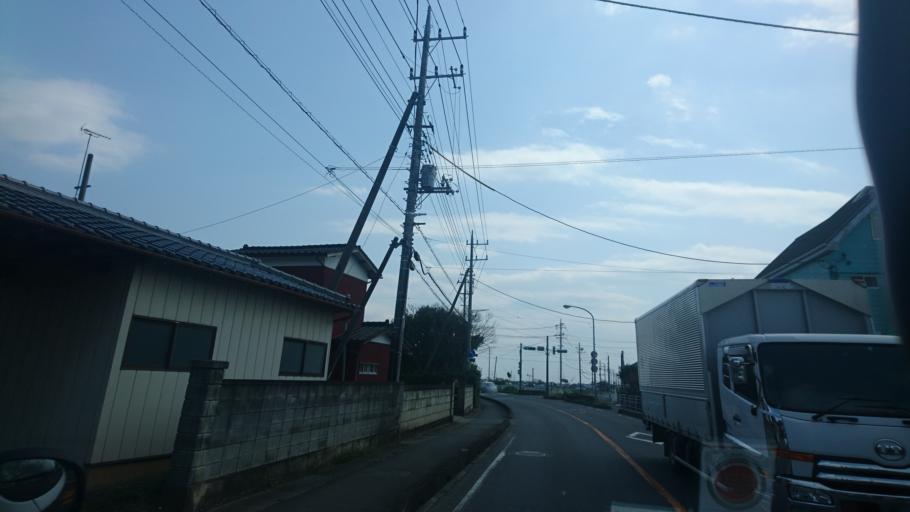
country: JP
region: Ibaraki
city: Yuki
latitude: 36.2847
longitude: 139.8966
